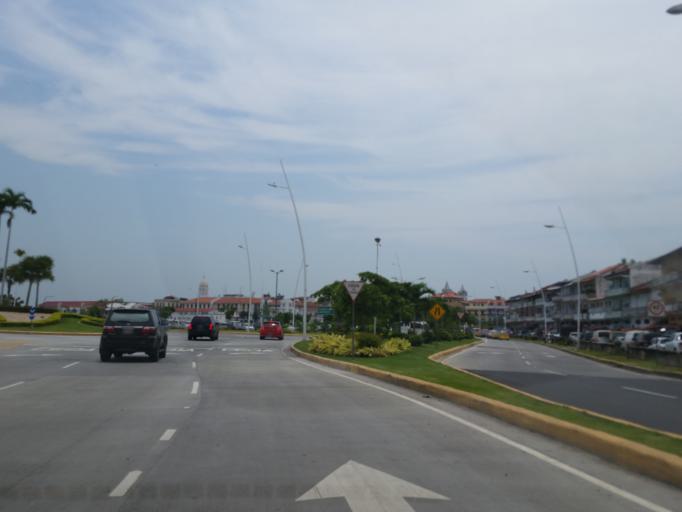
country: PA
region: Panama
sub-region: Distrito de Panama
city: Ancon
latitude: 8.9577
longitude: -79.5370
